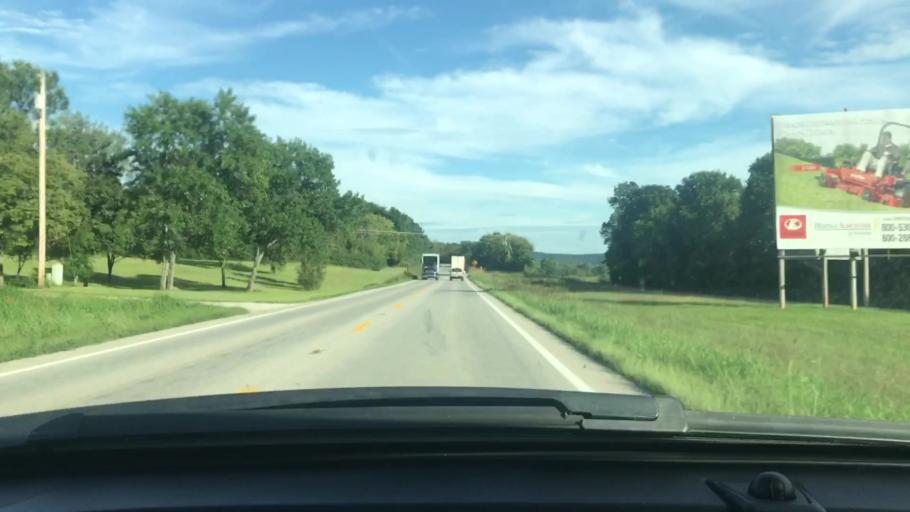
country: US
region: Arkansas
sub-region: Sharp County
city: Cherokee Village
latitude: 36.2998
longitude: -91.4408
